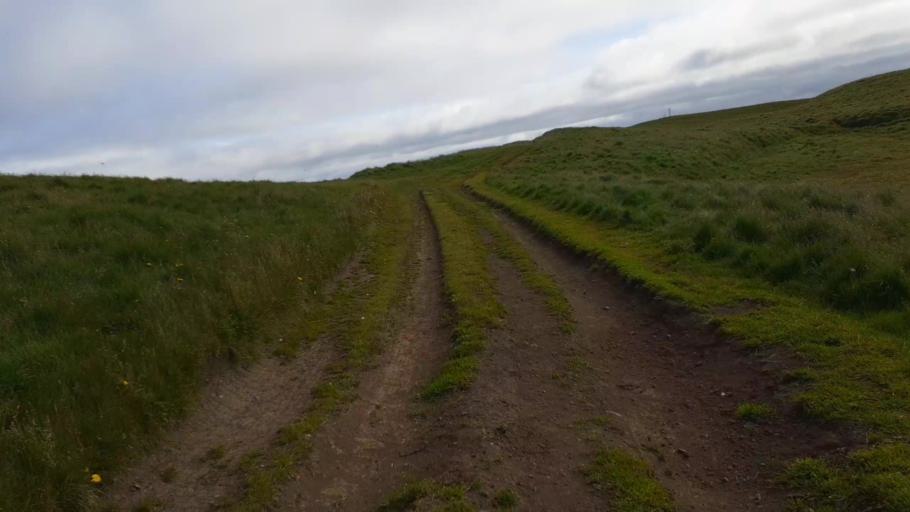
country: IS
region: Northeast
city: Dalvik
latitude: 66.5561
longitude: -18.0030
